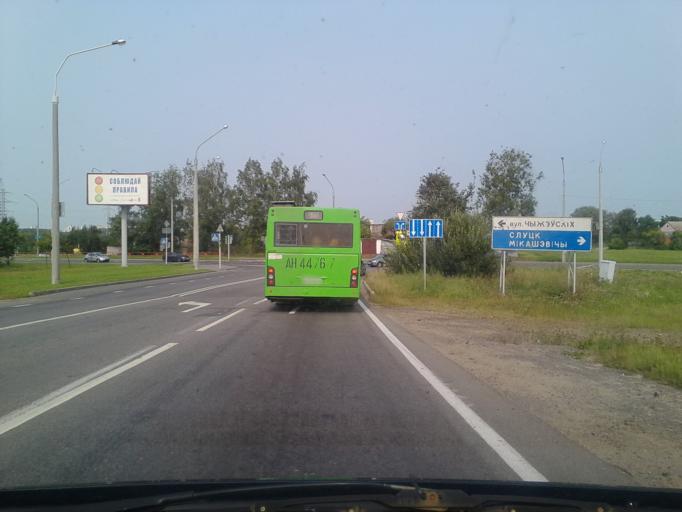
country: BY
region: Minsk
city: Machulishchy
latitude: 53.8350
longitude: 27.6008
